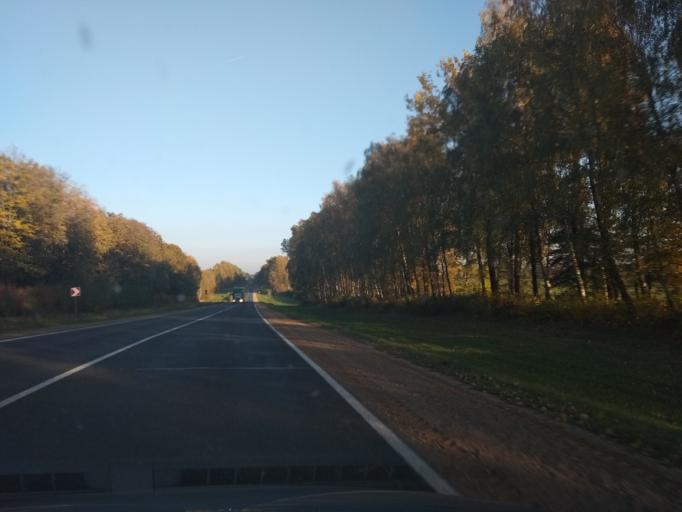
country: BY
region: Grodnenskaya
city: Vawkavysk
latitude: 53.1505
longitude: 24.5582
